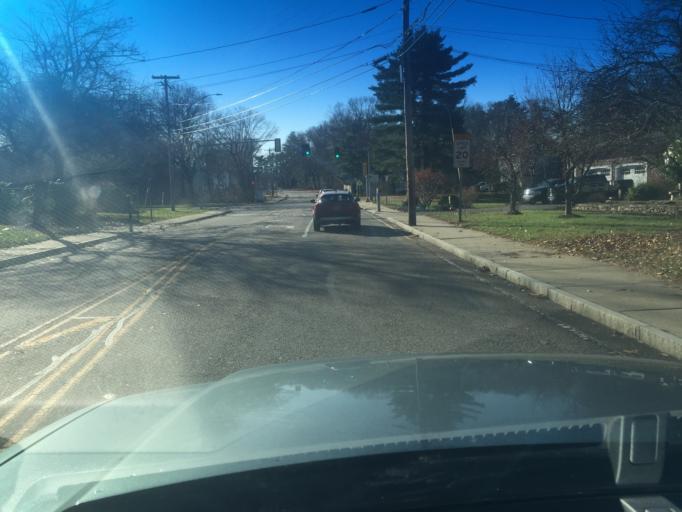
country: US
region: Massachusetts
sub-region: Norfolk County
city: Franklin
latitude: 42.1099
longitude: -71.4290
